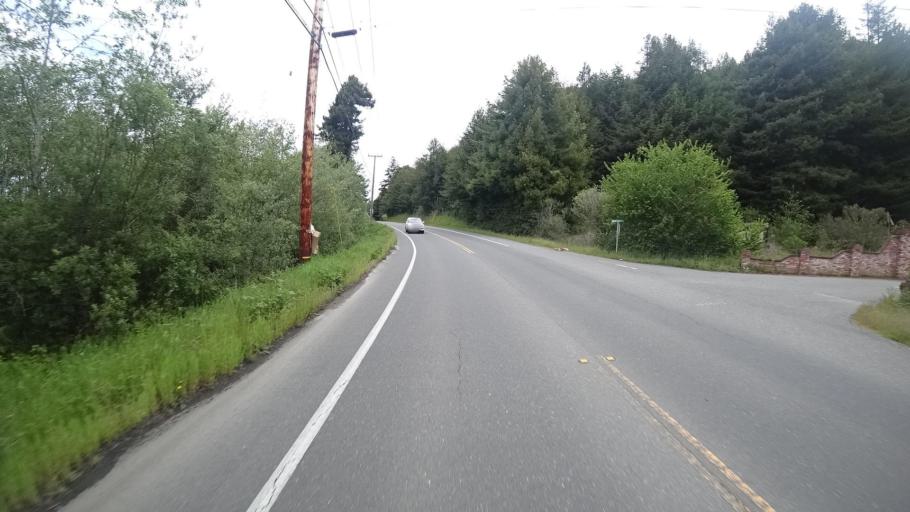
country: US
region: California
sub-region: Humboldt County
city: Bayside
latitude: 40.8227
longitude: -124.0786
